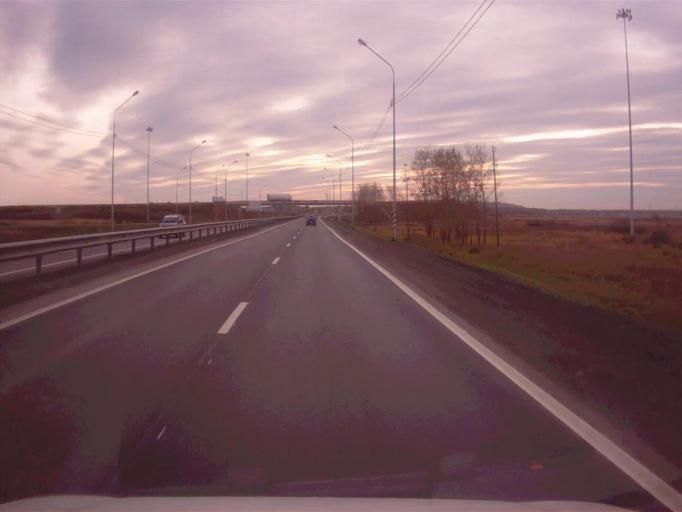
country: RU
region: Chelyabinsk
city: Roza
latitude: 54.9990
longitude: 61.4519
